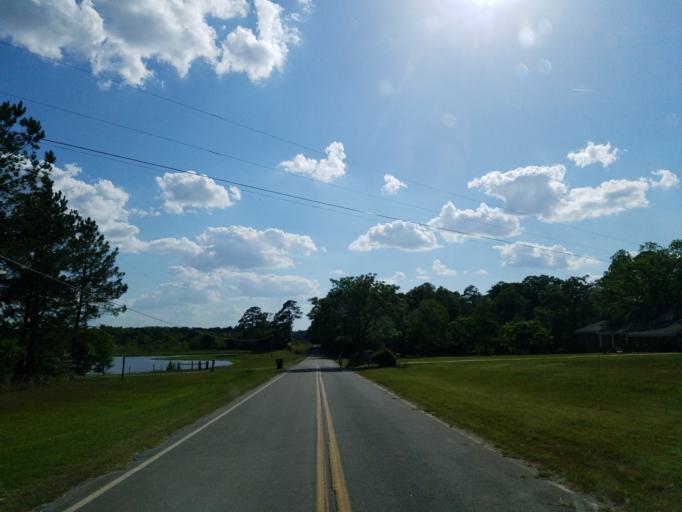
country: US
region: Georgia
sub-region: Crisp County
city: Cordele
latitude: 31.9955
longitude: -83.7524
